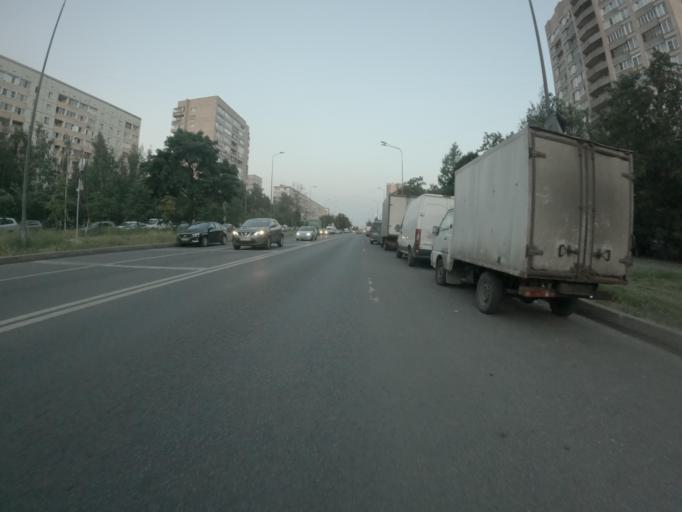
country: RU
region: St.-Petersburg
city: Krasnogvargeisky
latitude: 59.9185
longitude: 30.4818
